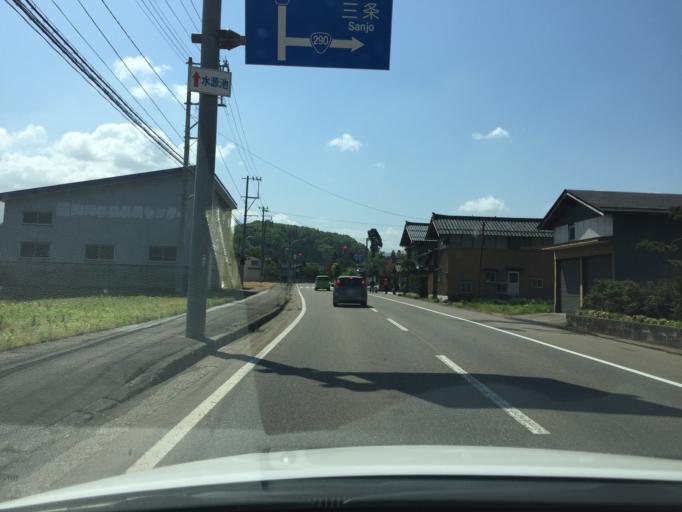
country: JP
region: Niigata
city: Kamo
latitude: 37.6097
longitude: 139.1050
